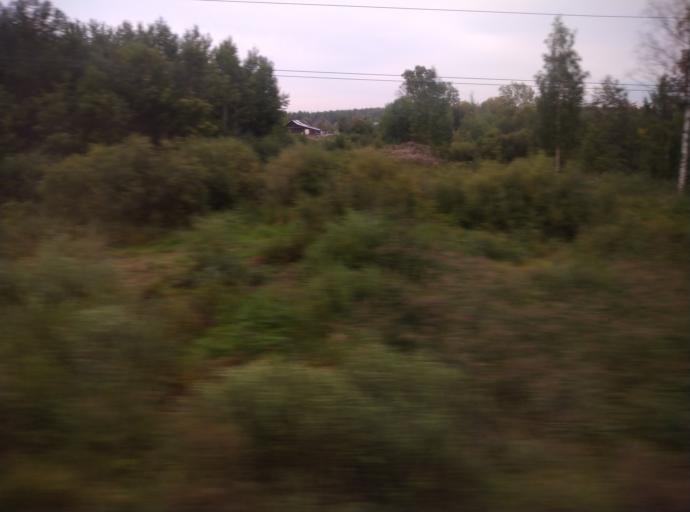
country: RU
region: Jaroslavl
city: Yaroslavl
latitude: 57.5652
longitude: 39.9112
